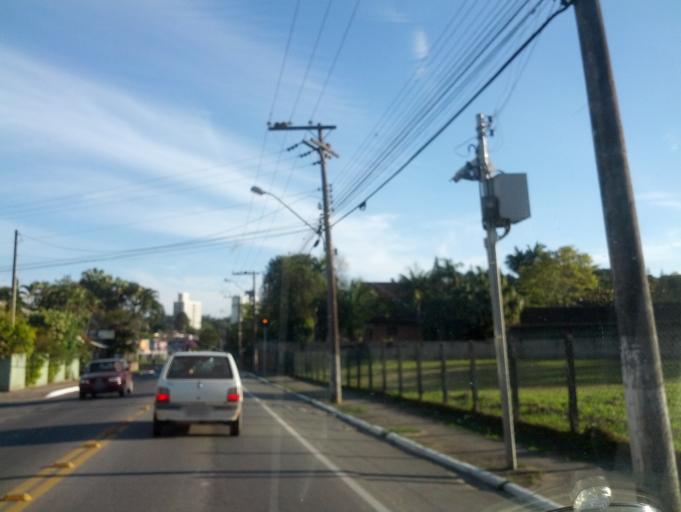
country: BR
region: Santa Catarina
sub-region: Indaial
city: Indaial
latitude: -26.8912
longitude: -49.2257
